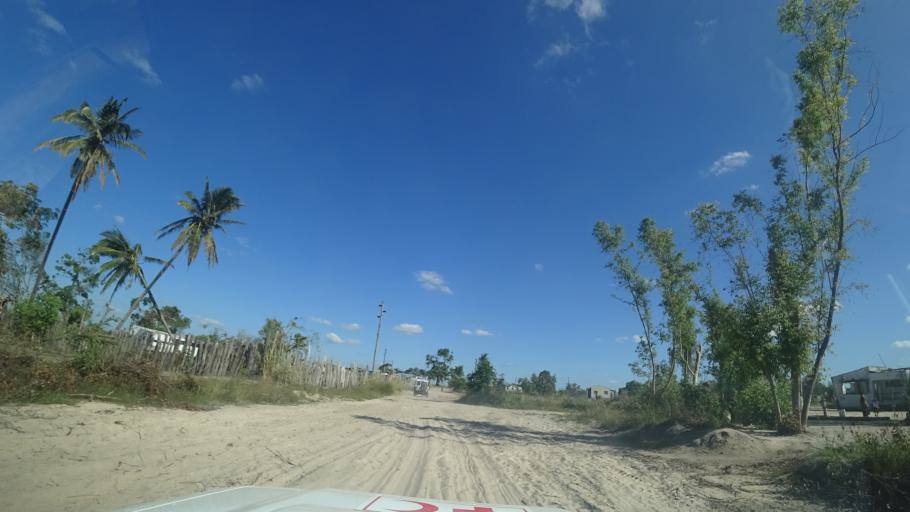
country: MZ
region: Sofala
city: Dondo
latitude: -19.5066
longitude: 34.6100
